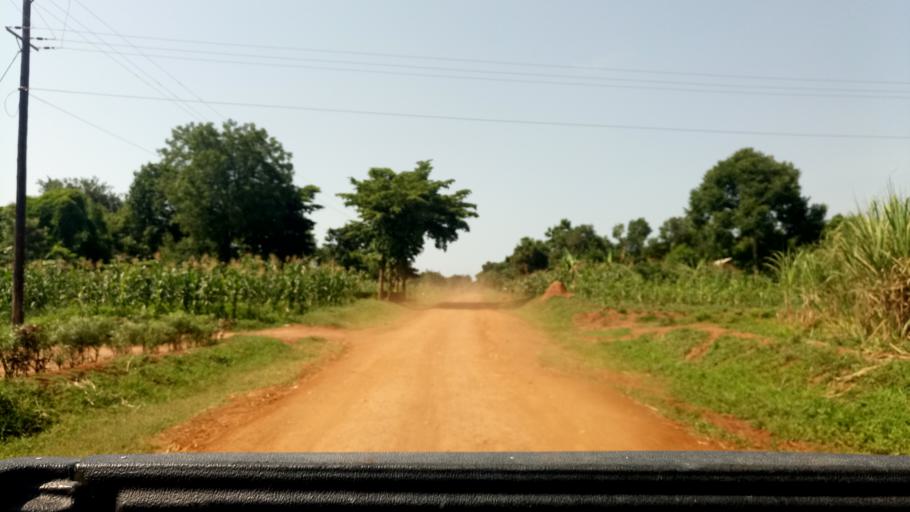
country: UG
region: Eastern Region
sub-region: Kaliro District
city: Kaliro
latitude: 0.9715
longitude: 33.4625
